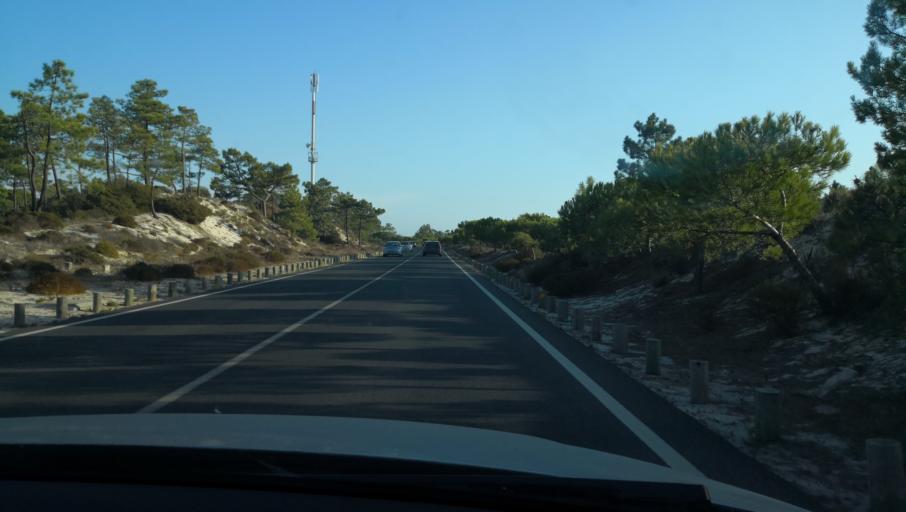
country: PT
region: Setubal
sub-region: Setubal
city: Setubal
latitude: 38.4719
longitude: -8.8845
